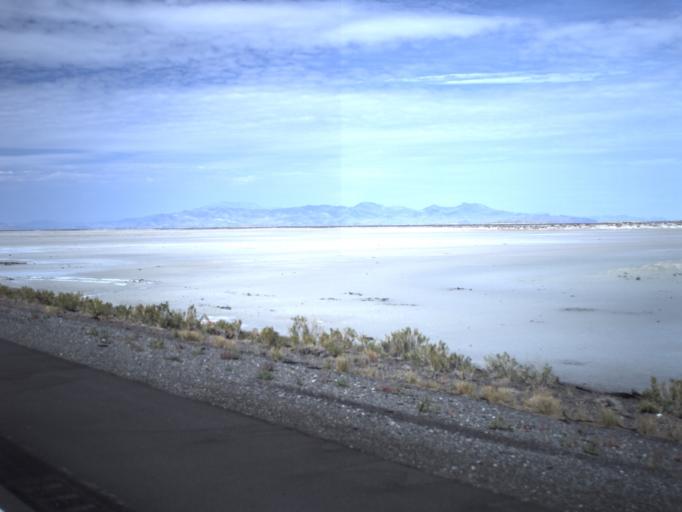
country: US
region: Utah
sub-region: Tooele County
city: Wendover
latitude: 40.7306
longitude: -113.4463
